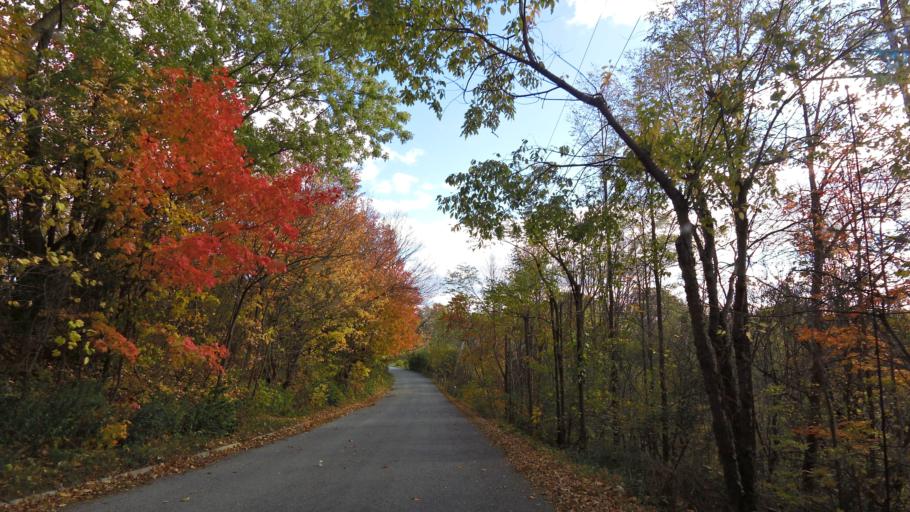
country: CA
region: Ontario
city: Burlington
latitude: 43.4406
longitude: -79.8405
